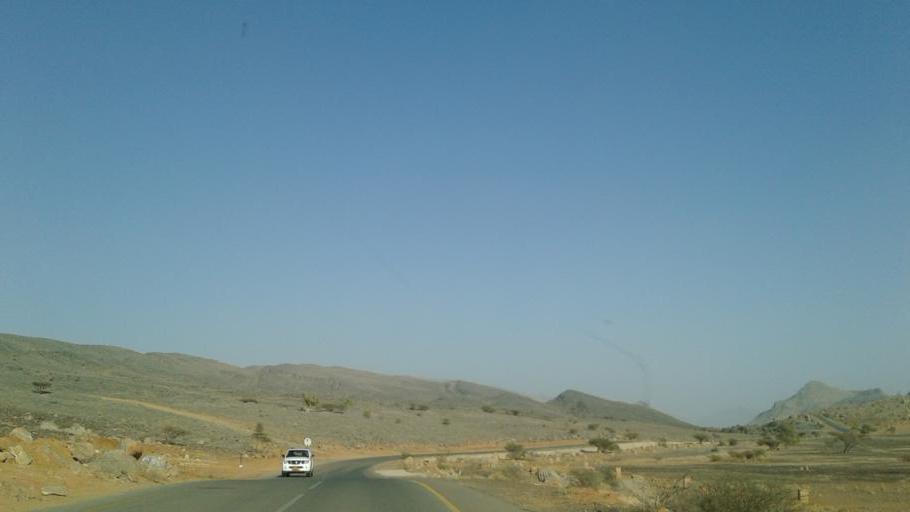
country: OM
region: Muhafazat ad Dakhiliyah
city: Bahla'
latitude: 23.0781
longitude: 57.3524
